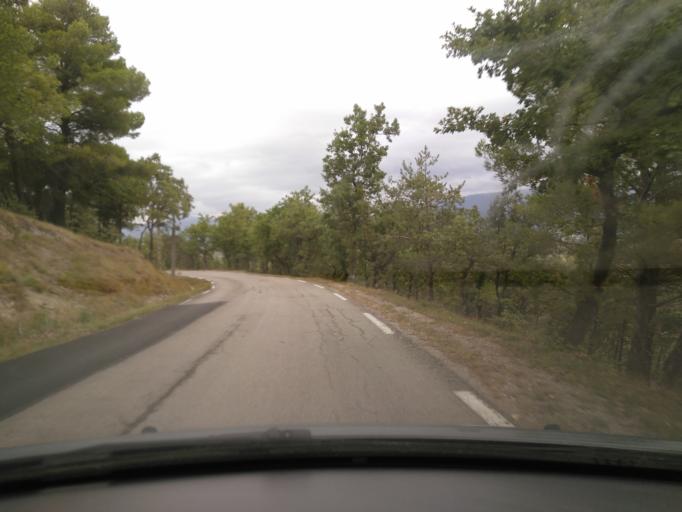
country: FR
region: Provence-Alpes-Cote d'Azur
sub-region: Departement du Vaucluse
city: Valreas
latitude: 44.3695
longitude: 5.0105
